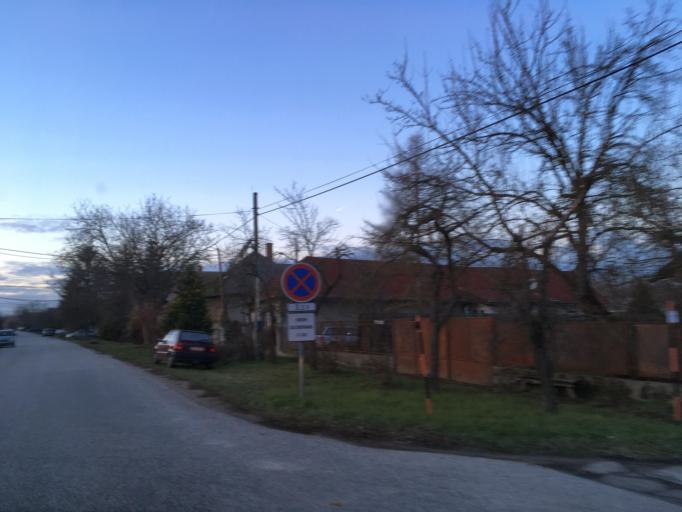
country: SK
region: Nitriansky
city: Svodin
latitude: 47.8725
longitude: 18.4586
